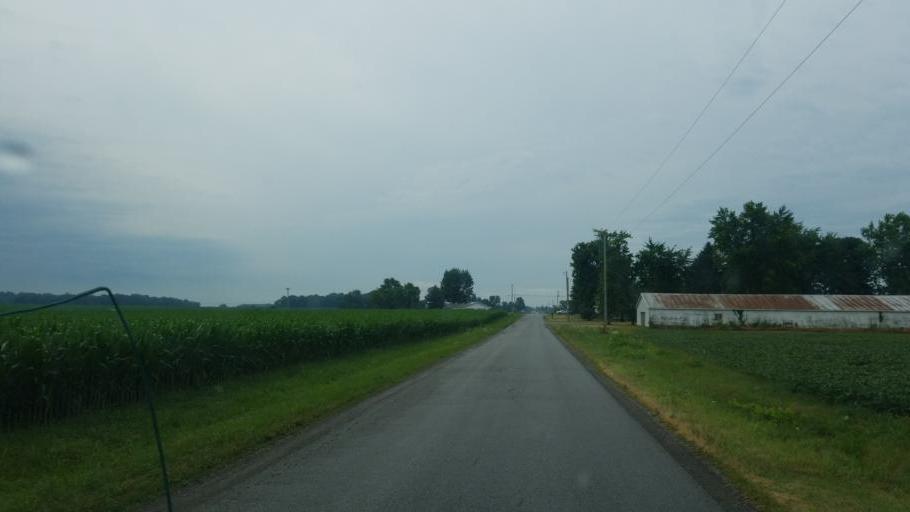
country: US
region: Ohio
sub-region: Williams County
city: Edgerton
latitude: 41.3854
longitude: -84.6698
